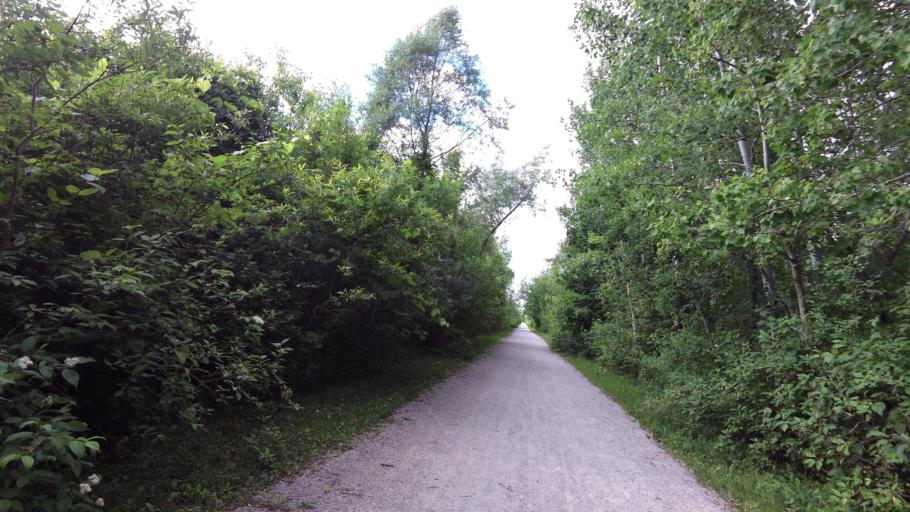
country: CA
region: Ontario
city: Brampton
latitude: 43.8009
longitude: -79.9318
